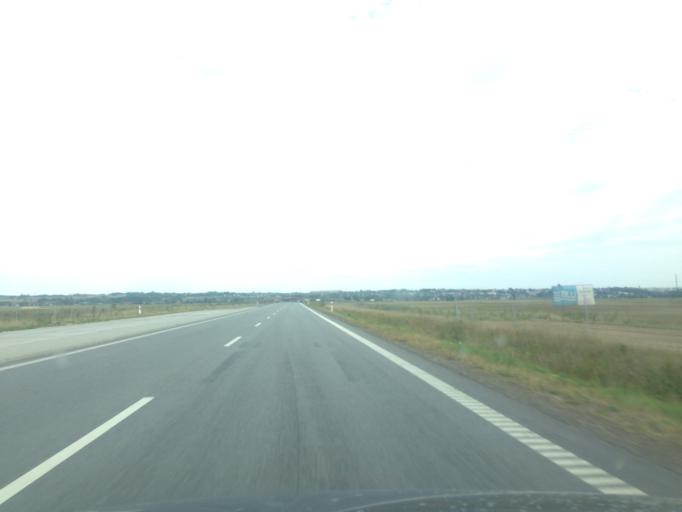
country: PL
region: Pomeranian Voivodeship
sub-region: Powiat kwidzynski
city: Kwidzyn
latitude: 53.7583
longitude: 18.8834
